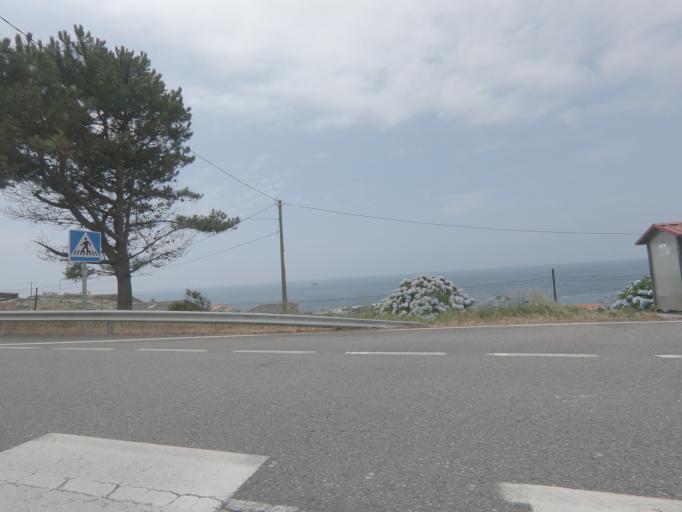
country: ES
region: Galicia
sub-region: Provincia de Pontevedra
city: O Rosal
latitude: 41.9516
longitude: -8.8826
